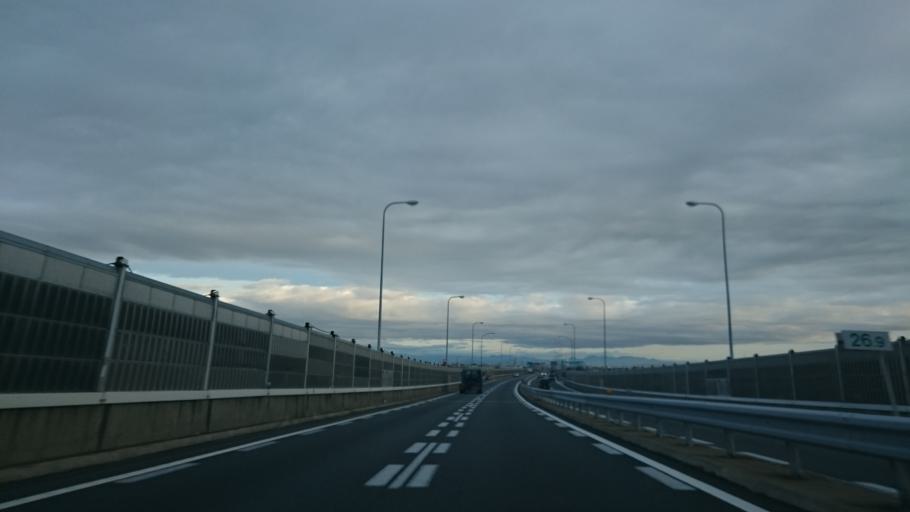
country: JP
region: Aichi
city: Kanie
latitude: 35.1704
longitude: 136.8162
